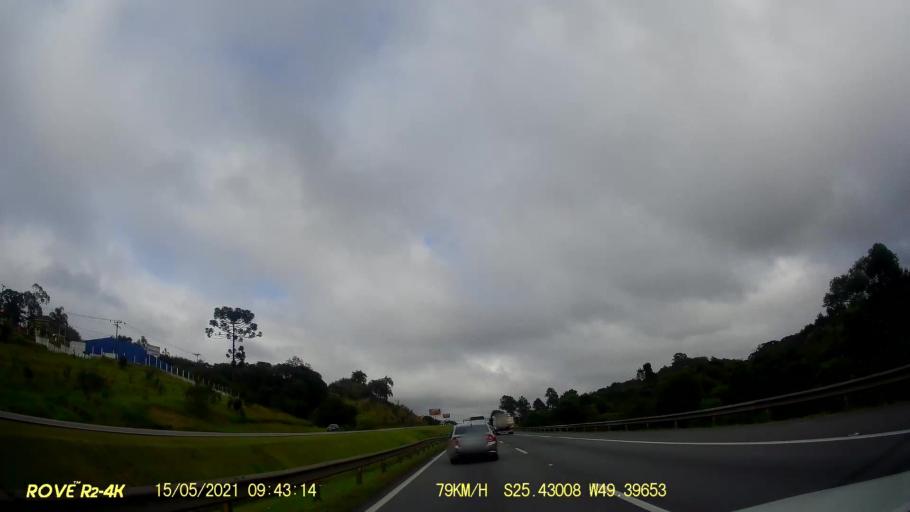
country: BR
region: Parana
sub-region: Curitiba
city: Curitiba
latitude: -25.4291
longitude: -49.3977
